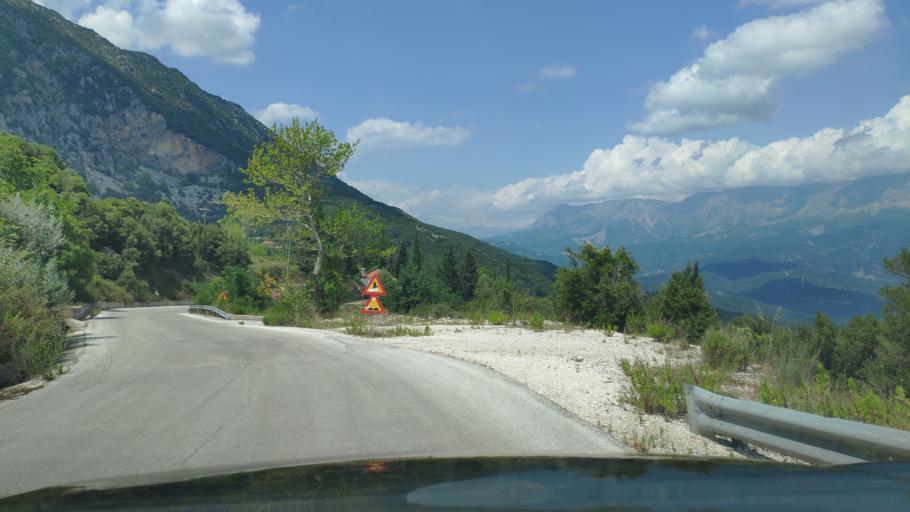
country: GR
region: Epirus
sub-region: Nomos Artas
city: Agios Dimitrios
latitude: 39.3395
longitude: 21.0065
